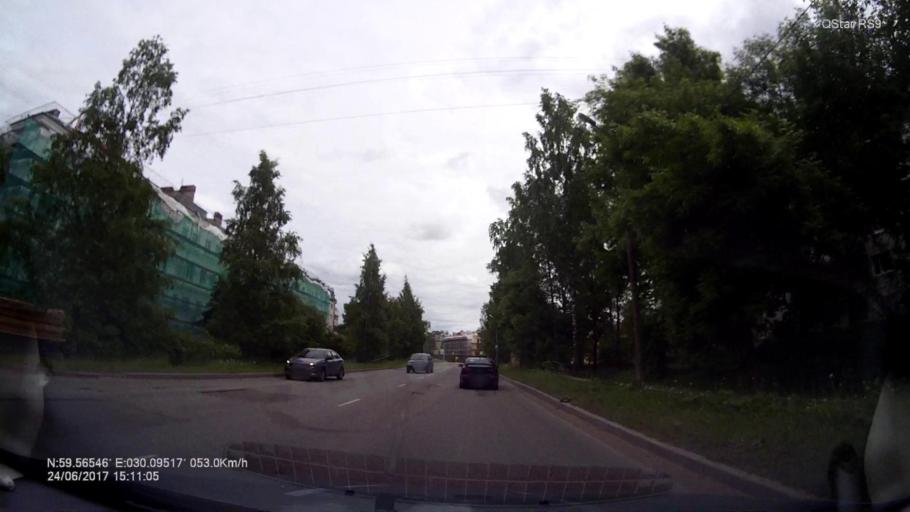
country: RU
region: Leningrad
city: Mariyenburg
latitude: 59.5653
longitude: 30.0956
